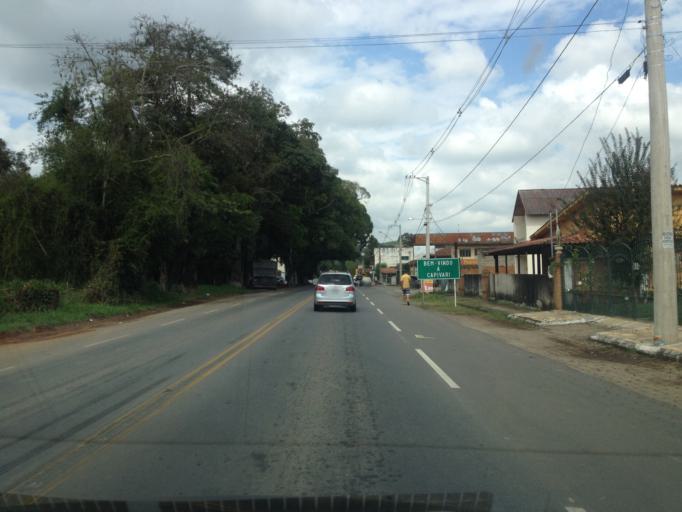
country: BR
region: Minas Gerais
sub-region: Itanhandu
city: Itanhandu
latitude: -22.2470
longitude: -44.9353
